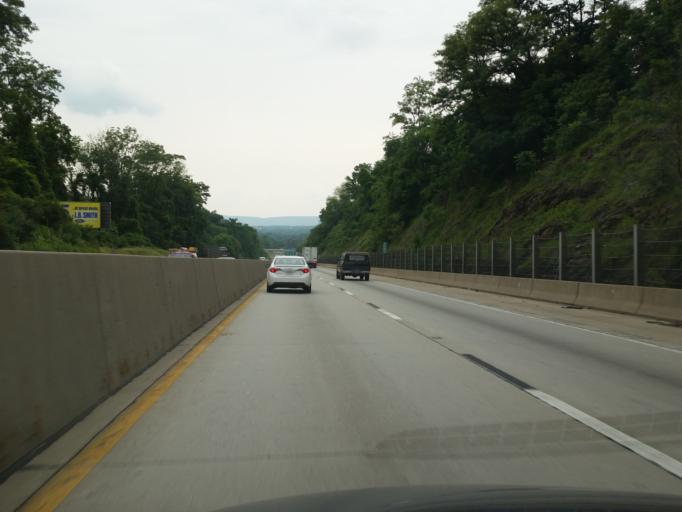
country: US
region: Pennsylvania
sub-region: Cumberland County
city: New Cumberland
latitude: 40.2000
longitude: -76.8663
